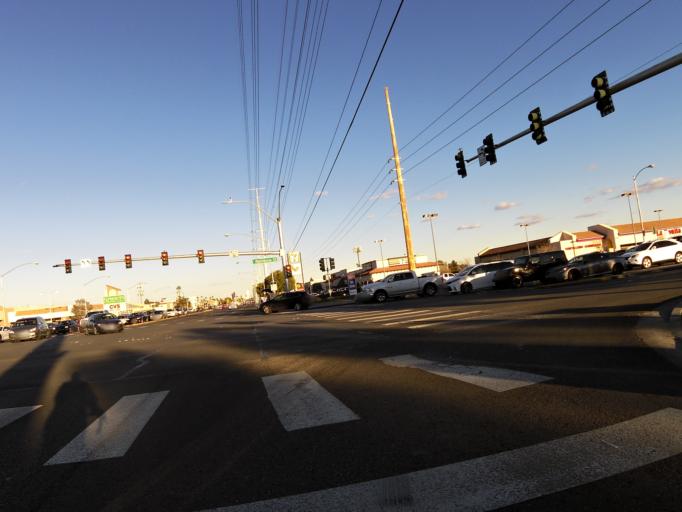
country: US
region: Nevada
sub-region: Clark County
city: Spring Valley
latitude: 36.1144
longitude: -115.2433
